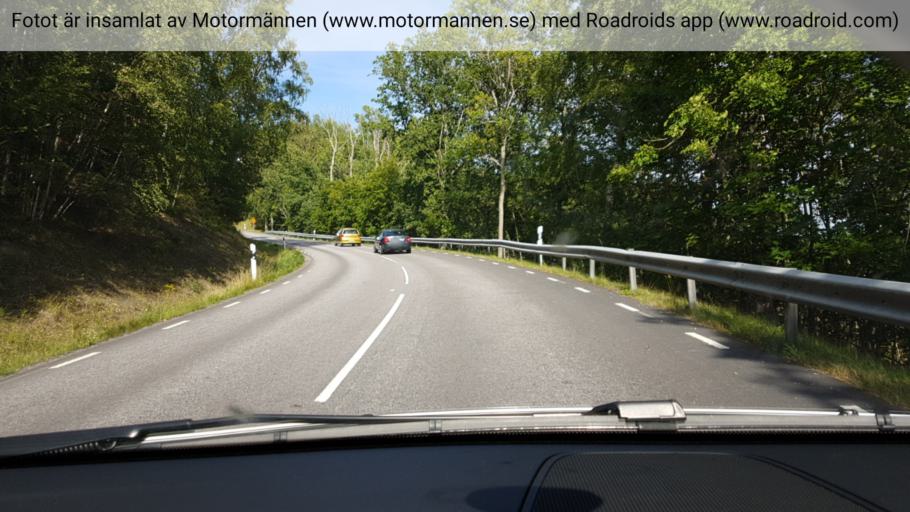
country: SE
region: Stockholm
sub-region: Sodertalje Kommun
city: Pershagen
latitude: 59.1027
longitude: 17.6322
